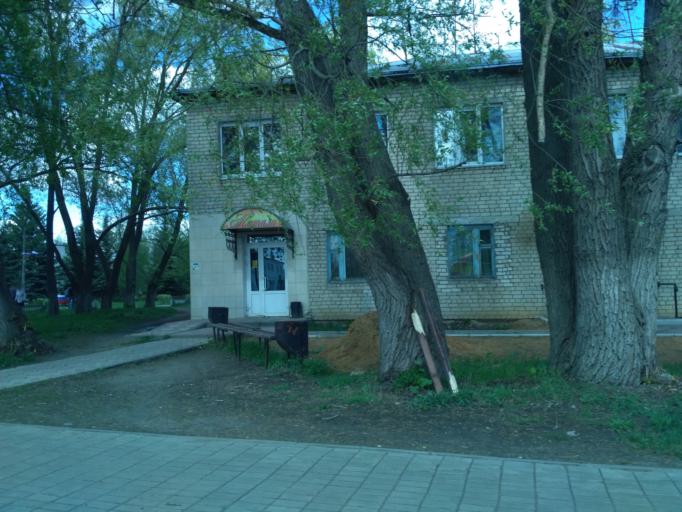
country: RU
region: Nizjnij Novgorod
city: Vad
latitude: 55.5308
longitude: 44.2102
